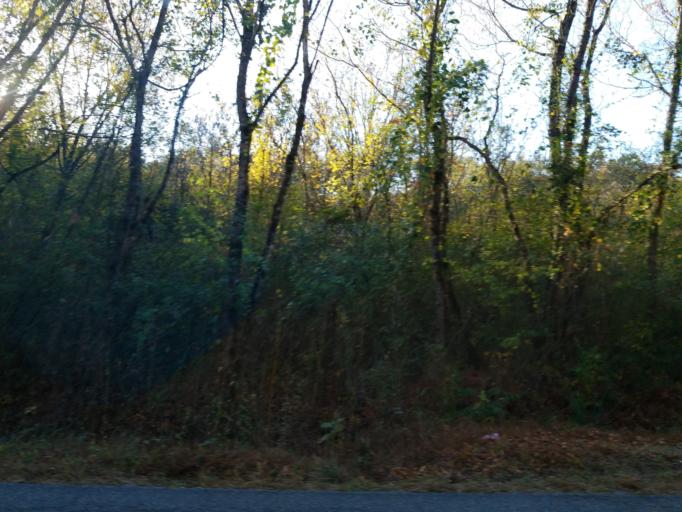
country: US
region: Georgia
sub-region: Bartow County
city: Euharlee
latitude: 34.2278
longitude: -84.9406
